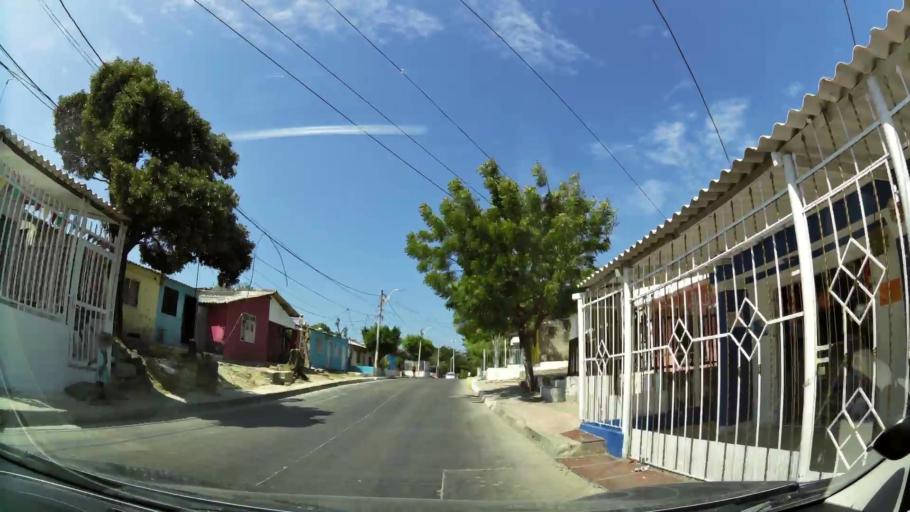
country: CO
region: Atlantico
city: Barranquilla
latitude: 10.9673
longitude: -74.8294
